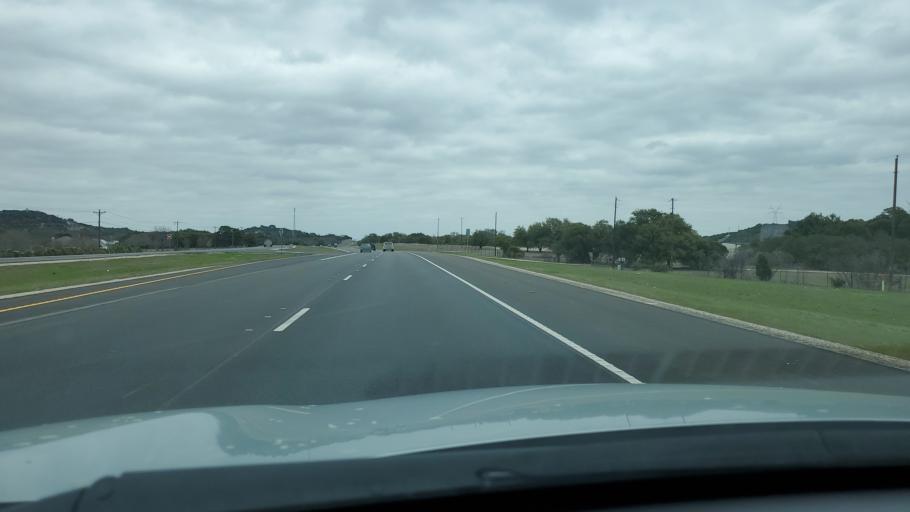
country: US
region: Texas
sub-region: Bell County
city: Killeen
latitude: 30.9923
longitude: -97.7639
